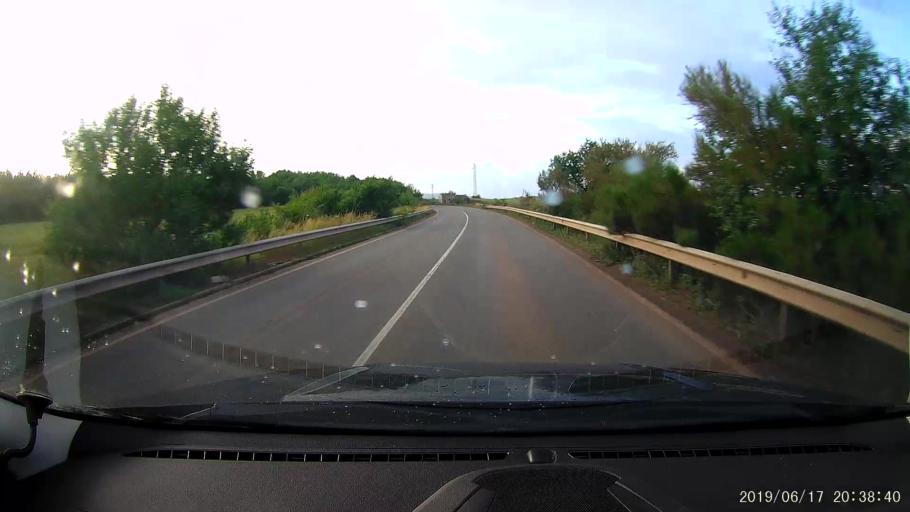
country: BG
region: Sofiya
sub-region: Obshtina Slivnitsa
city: Slivnitsa
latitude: 42.8756
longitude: 23.0185
